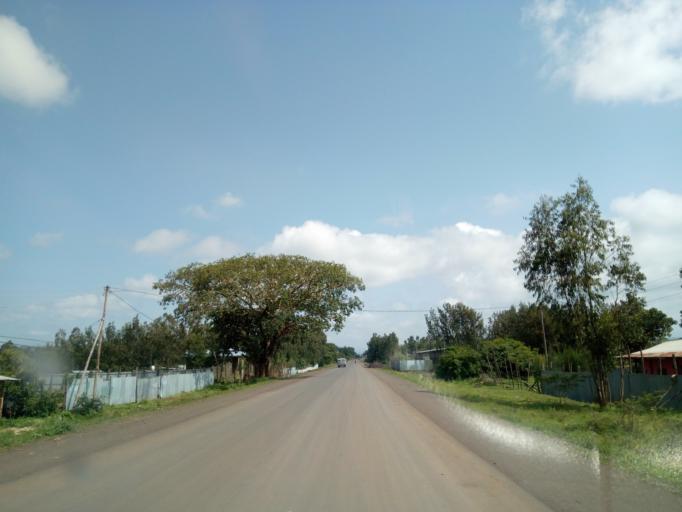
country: ET
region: Oromiya
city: Waliso
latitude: 8.5458
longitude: 37.9625
